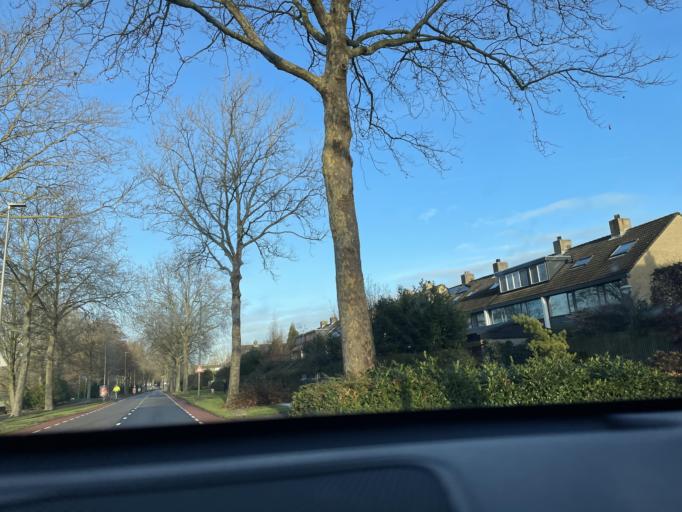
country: NL
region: South Holland
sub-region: Gemeente Krimpen aan den IJssel
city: Krimpen aan den IJssel
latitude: 51.9306
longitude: 4.6064
